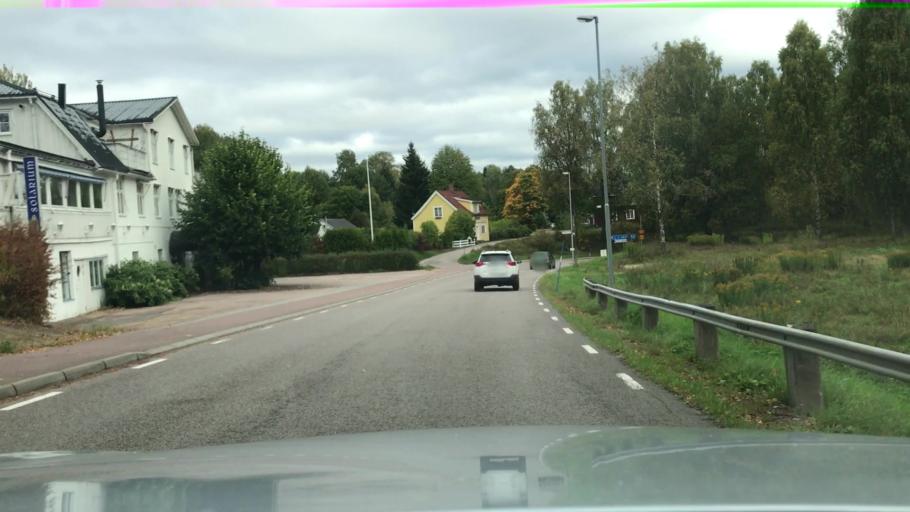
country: SE
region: Vaermland
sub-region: Munkfors Kommun
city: Munkfors
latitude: 59.8351
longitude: 13.5257
